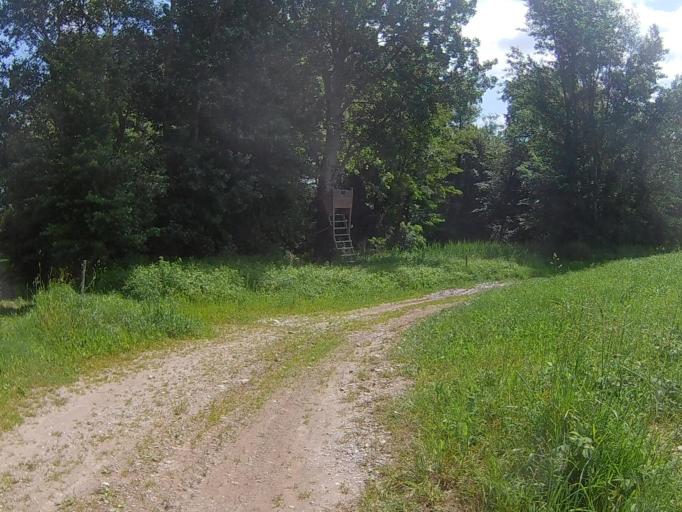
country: SI
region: Duplek
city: Zgornji Duplek
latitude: 46.5121
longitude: 15.7099
